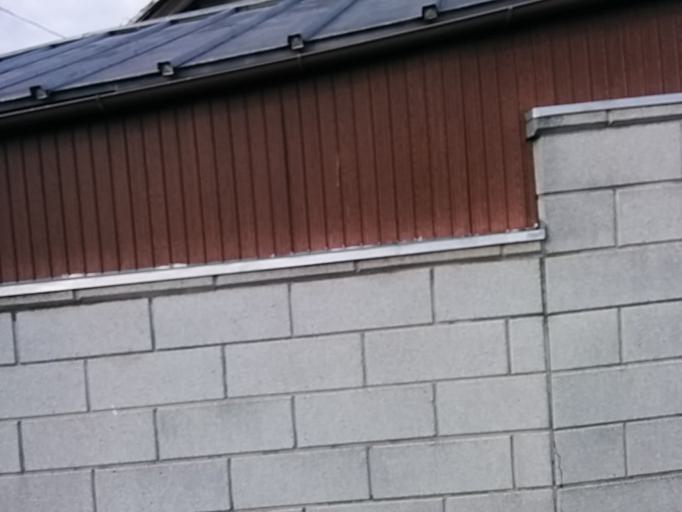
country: JP
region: Saitama
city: Kawagoe
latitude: 35.9092
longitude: 139.4928
